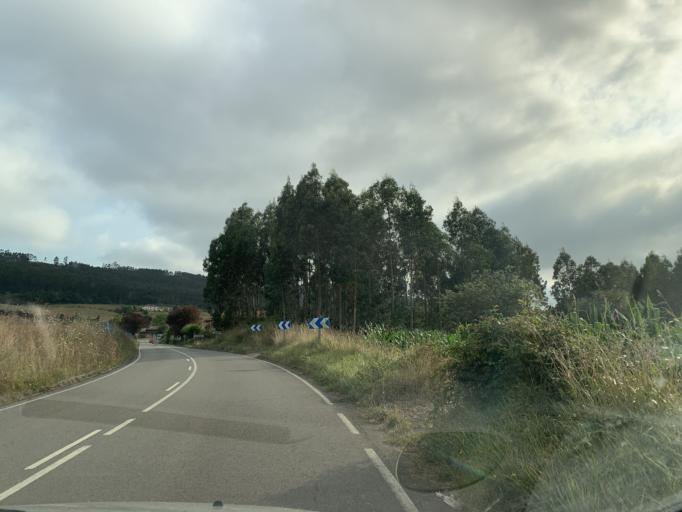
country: ES
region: Asturias
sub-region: Province of Asturias
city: Villaviciosa
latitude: 43.5231
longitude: -5.4379
